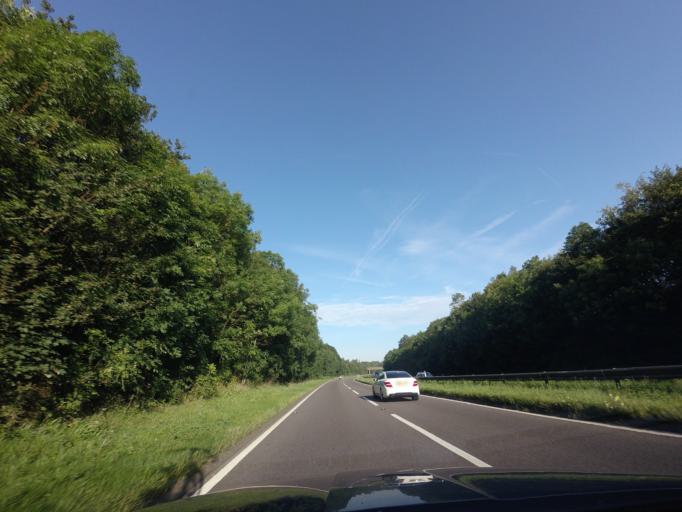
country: GB
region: England
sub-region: Derbyshire
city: Chesterfield
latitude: 53.2118
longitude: -1.3880
